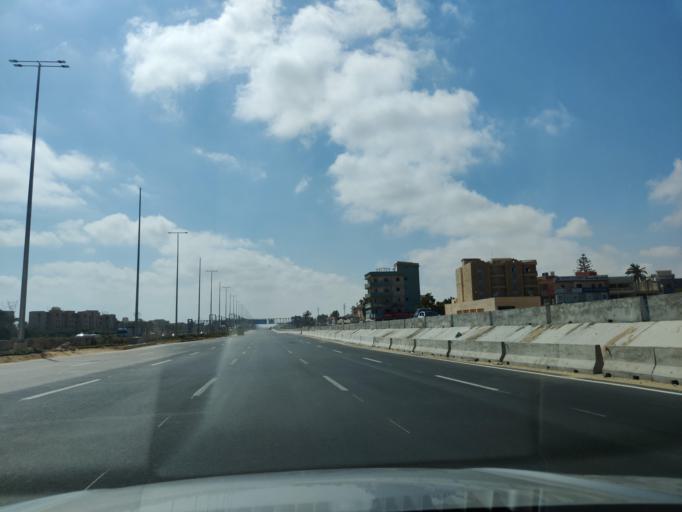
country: EG
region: Muhafazat Matruh
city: Al `Alamayn
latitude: 30.9716
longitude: 28.7377
